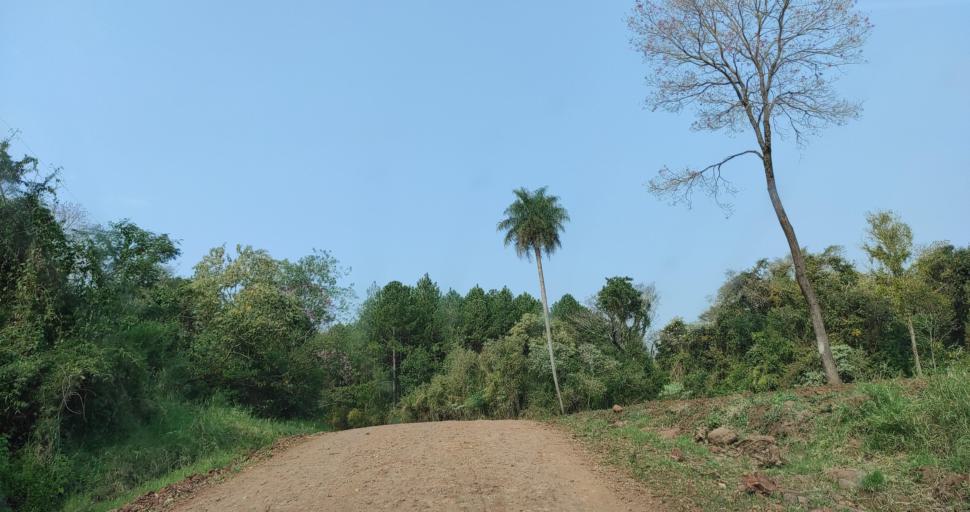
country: AR
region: Misiones
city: Cerro Azul
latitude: -27.6266
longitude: -55.5323
